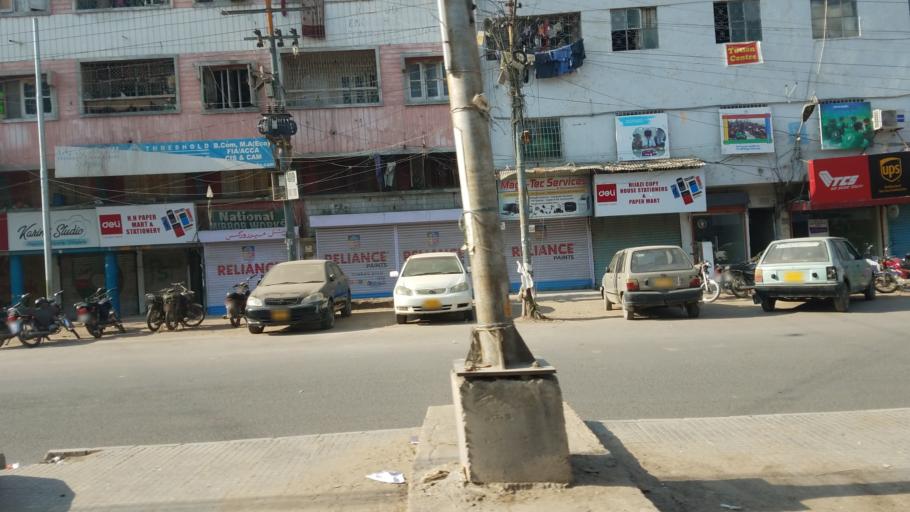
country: PK
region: Sindh
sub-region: Karachi District
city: Karachi
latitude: 24.9170
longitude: 67.0553
